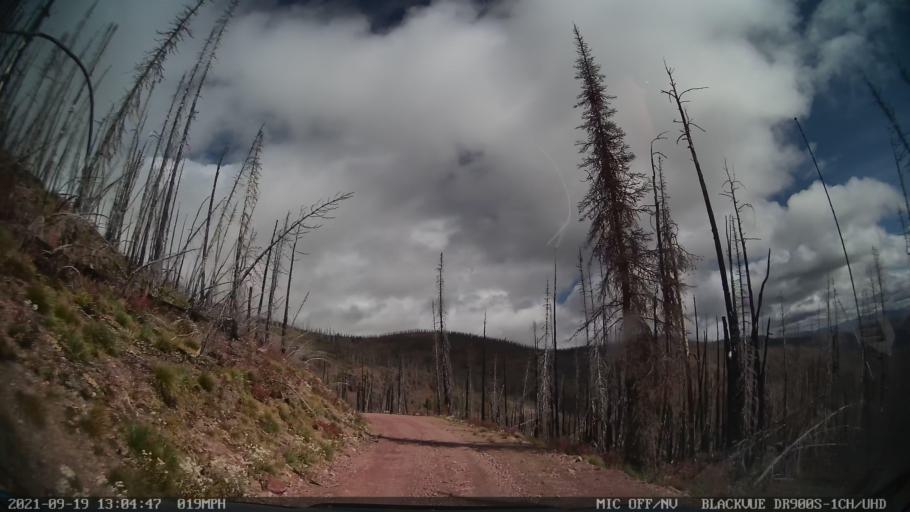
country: US
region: Montana
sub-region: Missoula County
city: Seeley Lake
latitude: 47.1868
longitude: -113.3519
